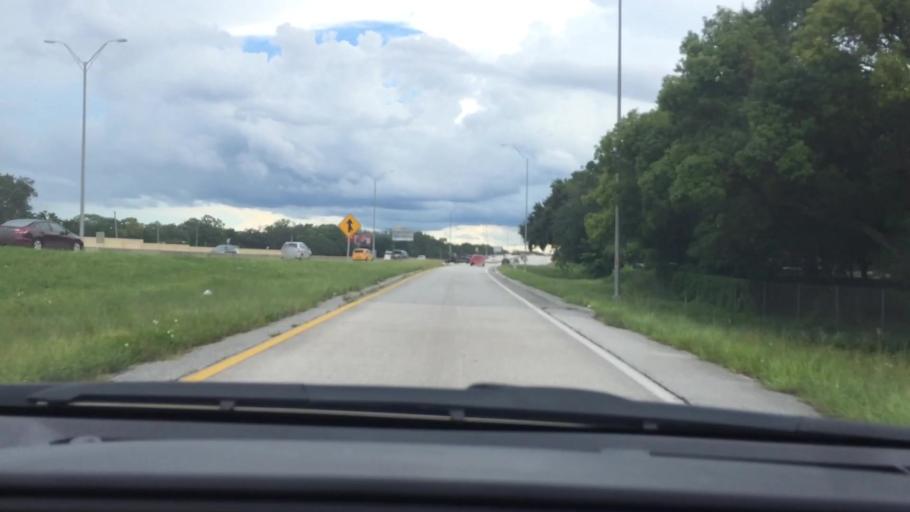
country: US
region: Florida
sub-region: Hillsborough County
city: University
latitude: 28.0568
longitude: -82.4543
